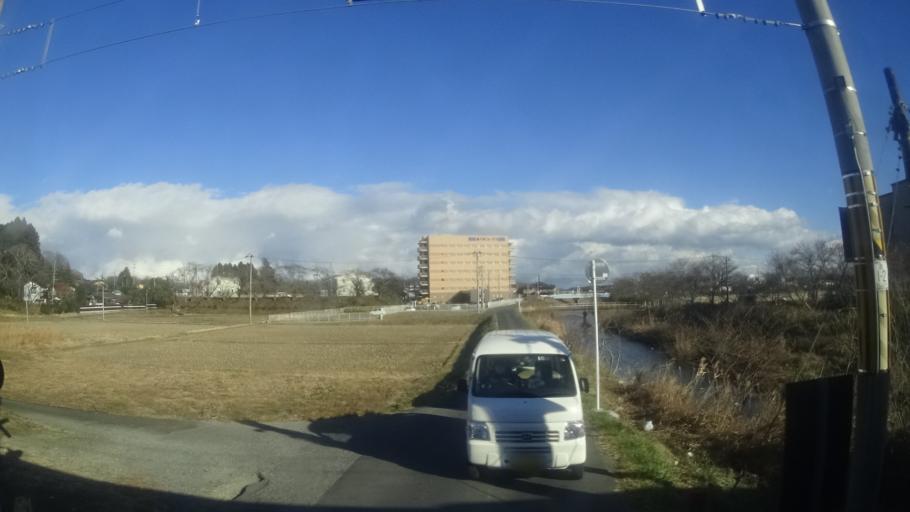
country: JP
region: Miyagi
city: Marumori
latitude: 37.8076
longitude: 140.9242
